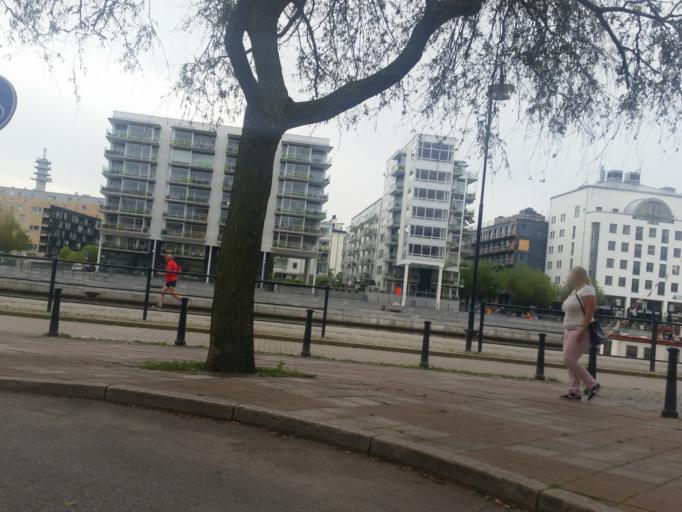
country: SE
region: Stockholm
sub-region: Stockholms Kommun
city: OEstermalm
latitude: 59.3058
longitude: 18.0883
